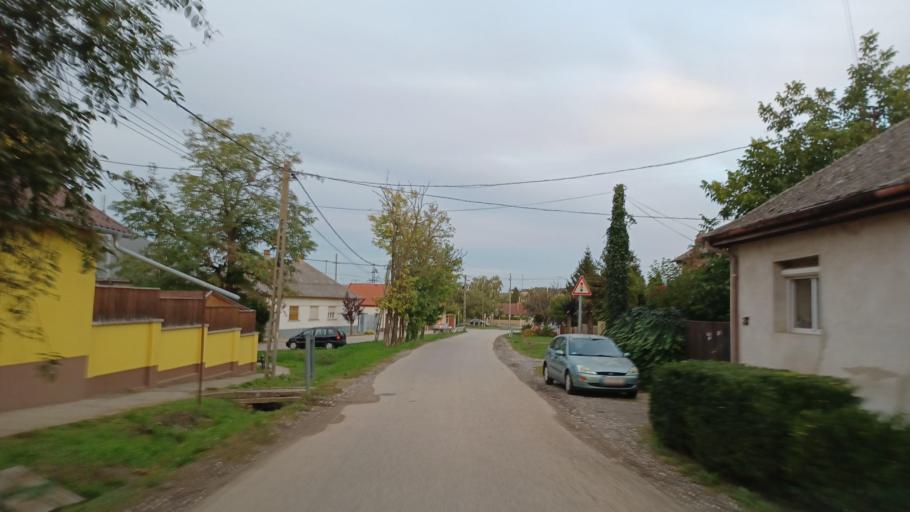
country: HU
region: Tolna
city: Dunafoldvar
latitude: 46.8017
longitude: 18.9153
